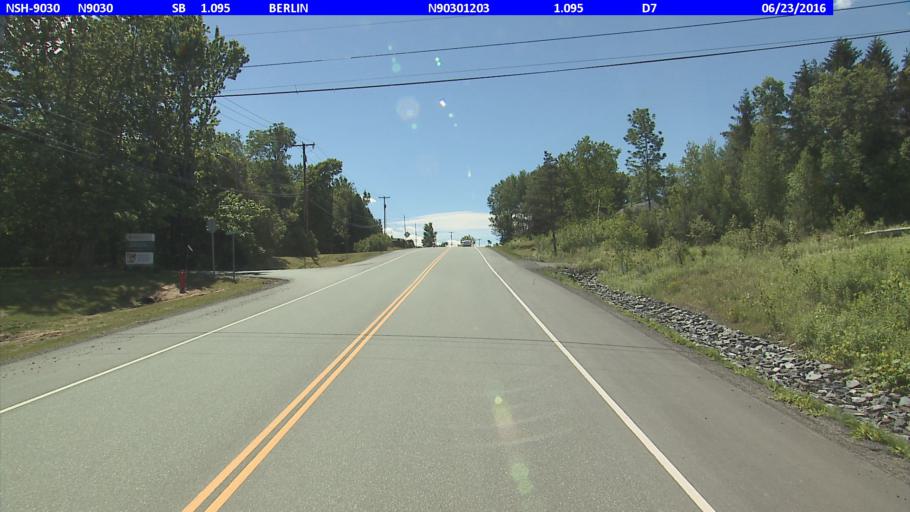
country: US
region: Vermont
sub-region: Washington County
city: Montpelier
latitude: 44.2170
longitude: -72.5584
